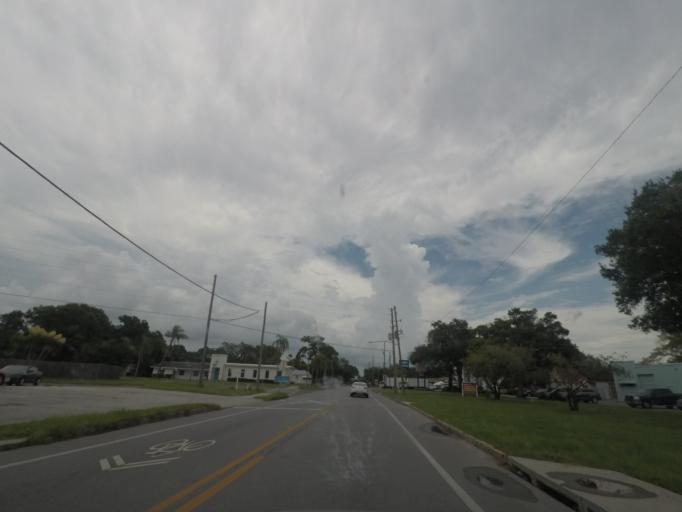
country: US
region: Florida
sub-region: Pinellas County
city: Lealman
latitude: 27.7992
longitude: -82.6683
